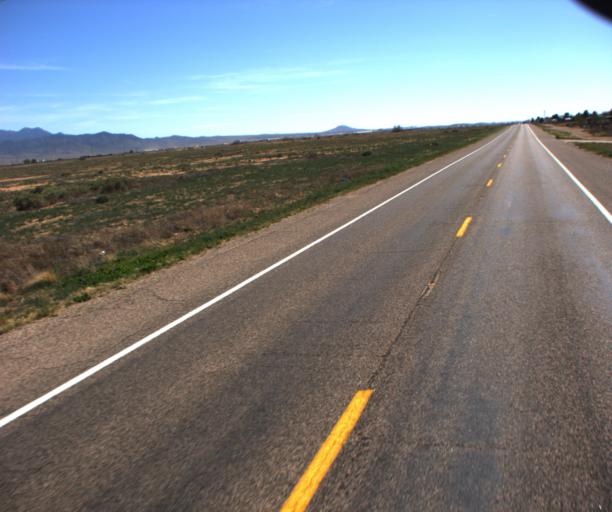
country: US
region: Arizona
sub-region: Mohave County
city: New Kingman-Butler
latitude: 35.2986
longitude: -113.9330
